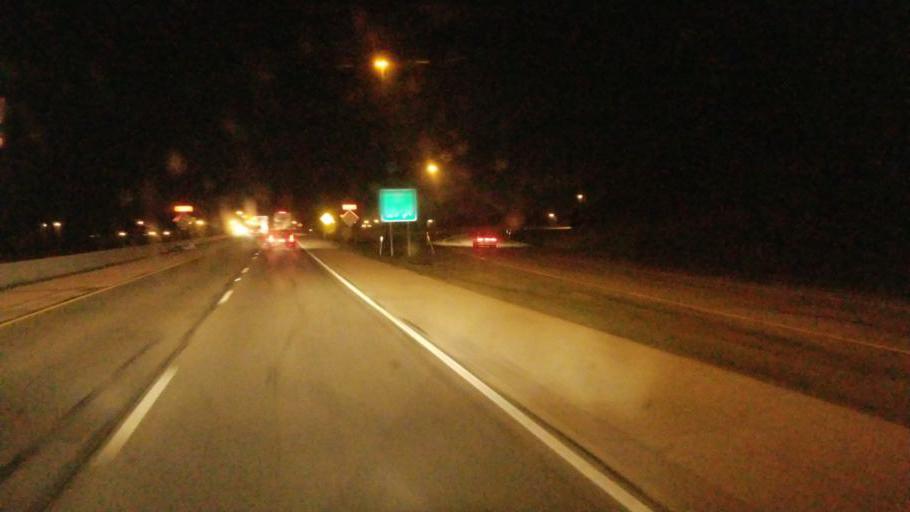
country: US
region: Indiana
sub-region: Allen County
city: Leo-Cedarville
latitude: 41.1581
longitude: -85.0576
